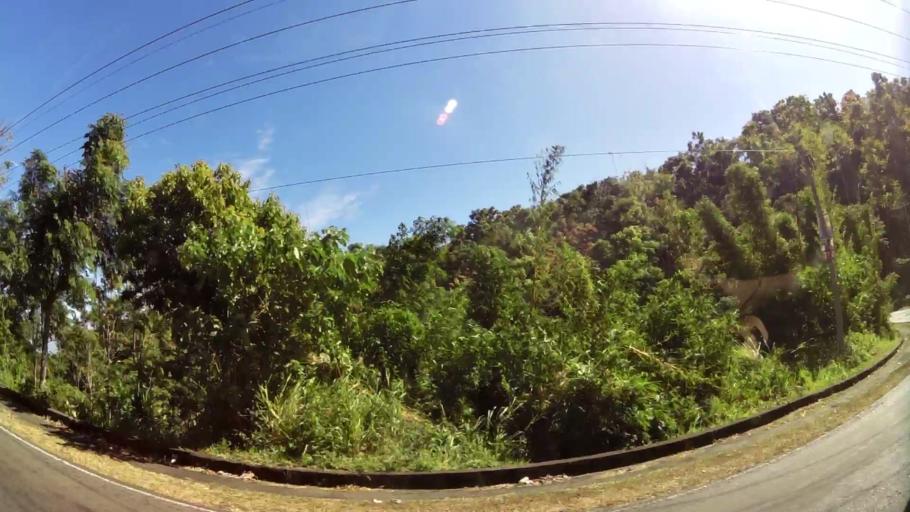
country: SV
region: Ahuachapan
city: Concepcion de Ataco
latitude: 13.8944
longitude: -89.8367
